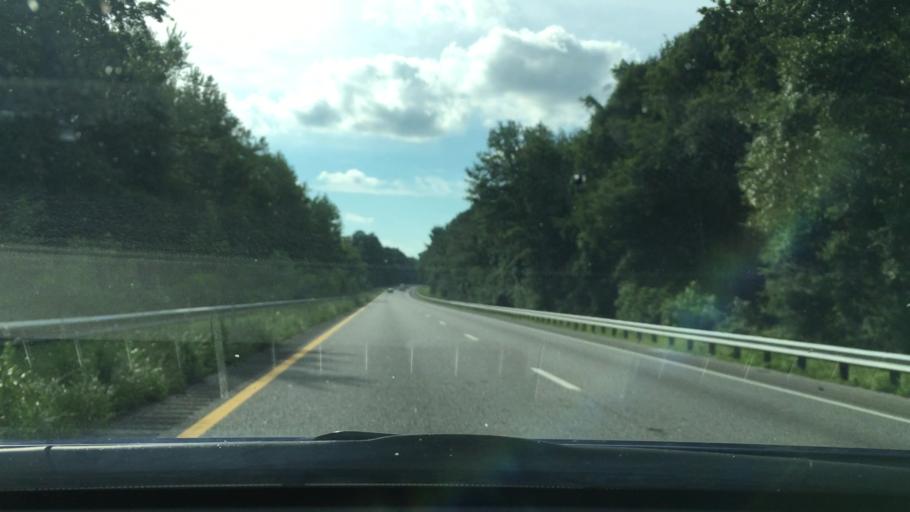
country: US
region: South Carolina
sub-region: Dorchester County
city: Ridgeville
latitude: 33.1515
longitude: -80.3399
